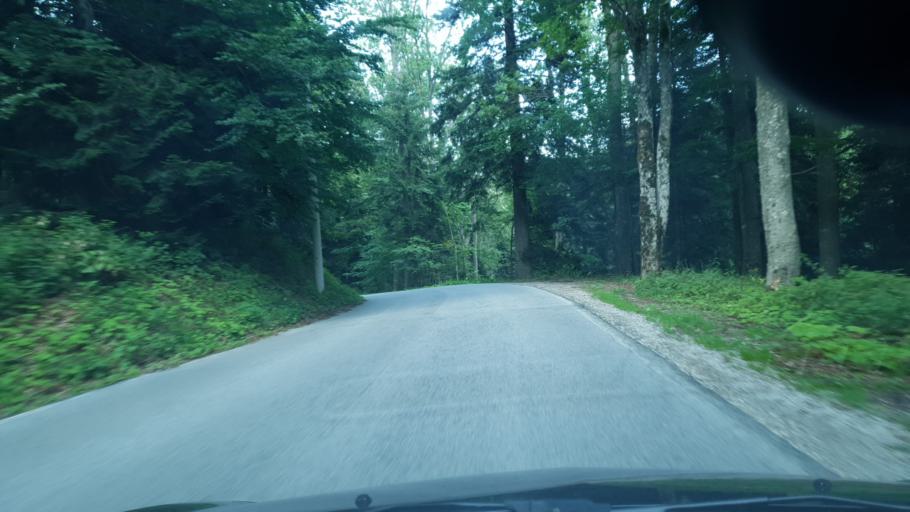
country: HR
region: Grad Zagreb
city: Kasina
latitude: 45.9044
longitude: 15.9635
